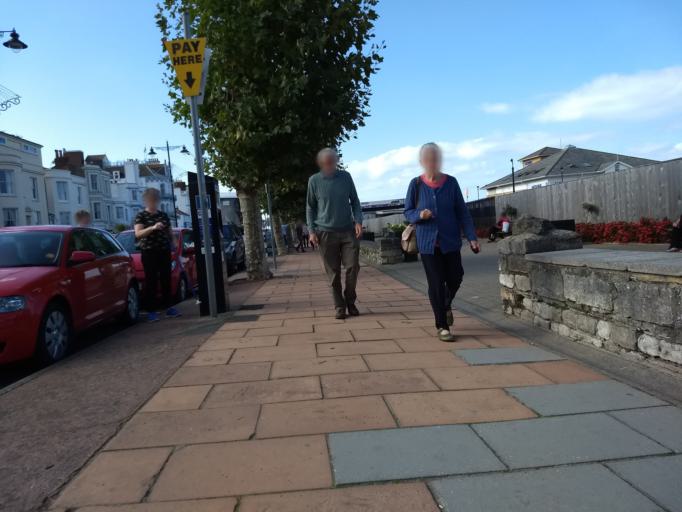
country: GB
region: England
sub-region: Isle of Wight
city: Ryde
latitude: 50.7320
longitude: -1.1575
